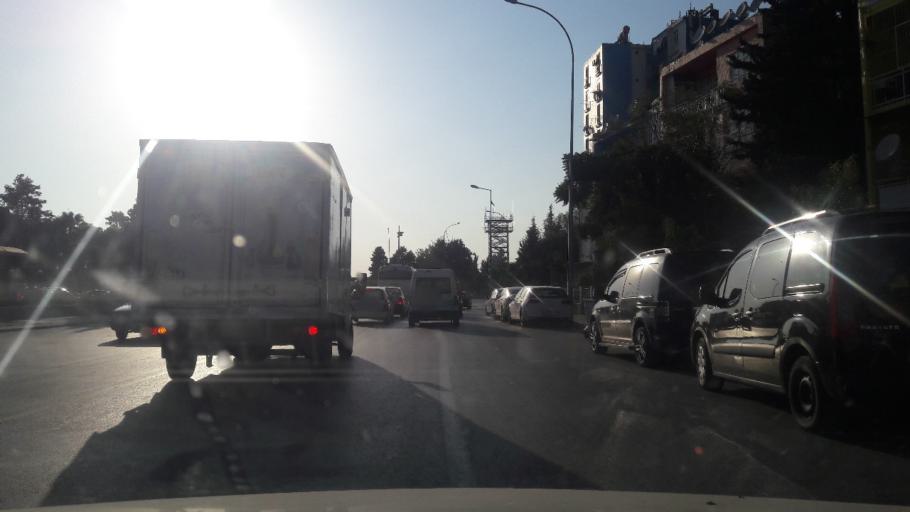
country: TR
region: Adana
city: Seyhan
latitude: 36.9874
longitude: 35.2993
